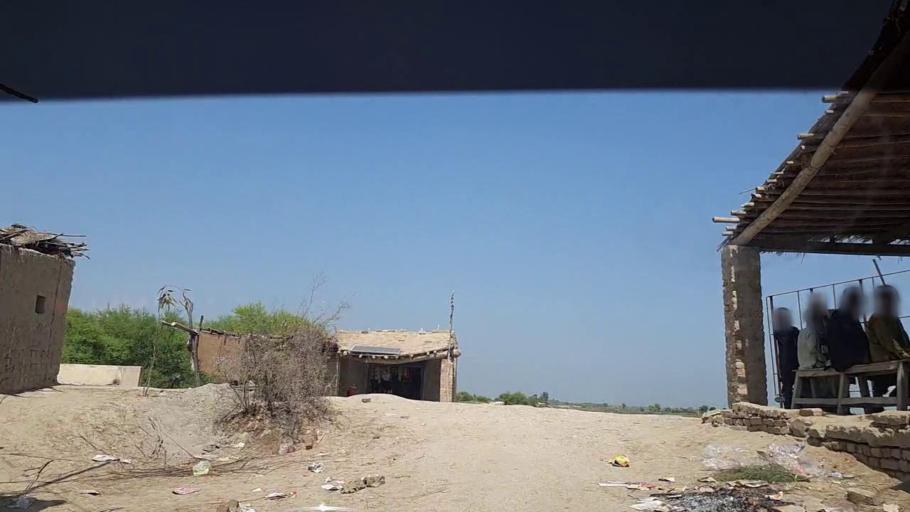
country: PK
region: Sindh
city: Kandhkot
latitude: 28.1895
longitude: 69.1625
